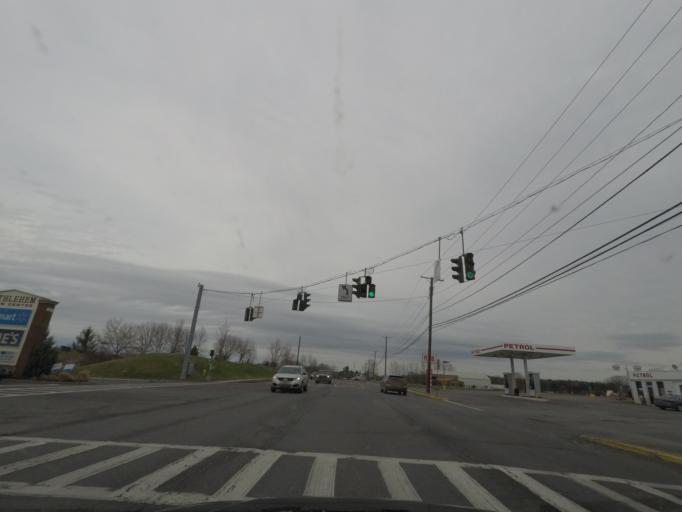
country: US
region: New York
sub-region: Albany County
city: Delmar
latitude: 42.6091
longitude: -73.7893
